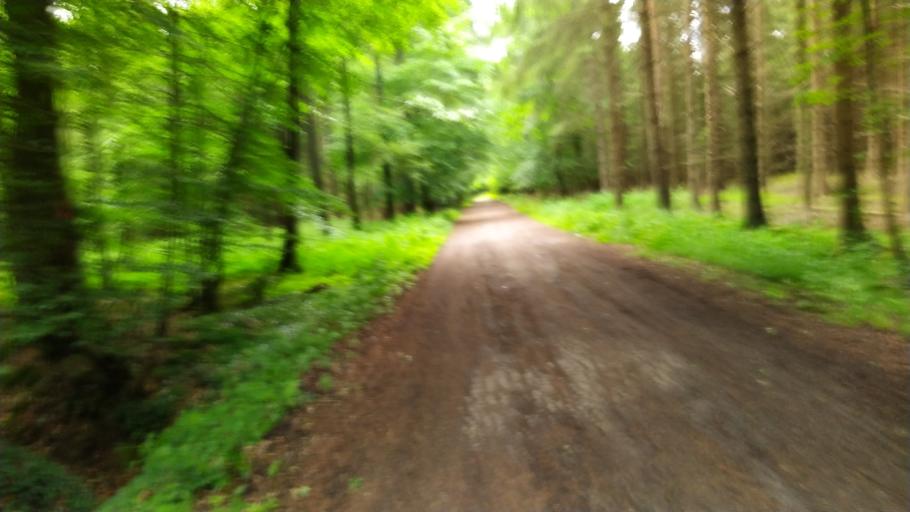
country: DE
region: Lower Saxony
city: Deinstedt
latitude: 53.4403
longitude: 9.2026
